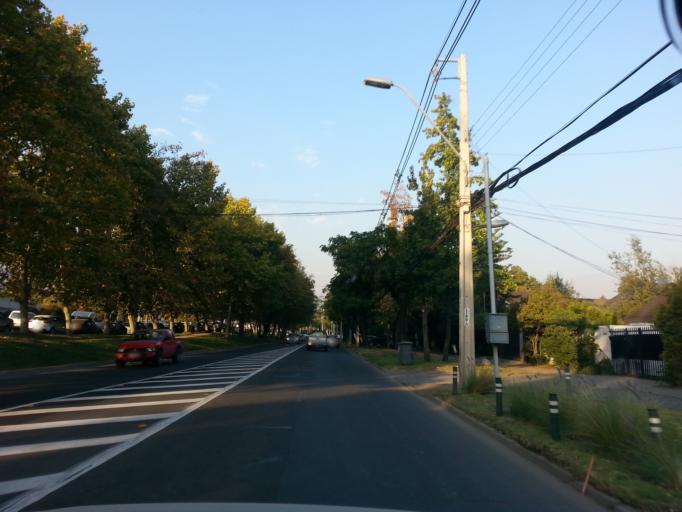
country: CL
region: Santiago Metropolitan
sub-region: Provincia de Santiago
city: Villa Presidente Frei, Nunoa, Santiago, Chile
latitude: -33.3828
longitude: -70.5830
